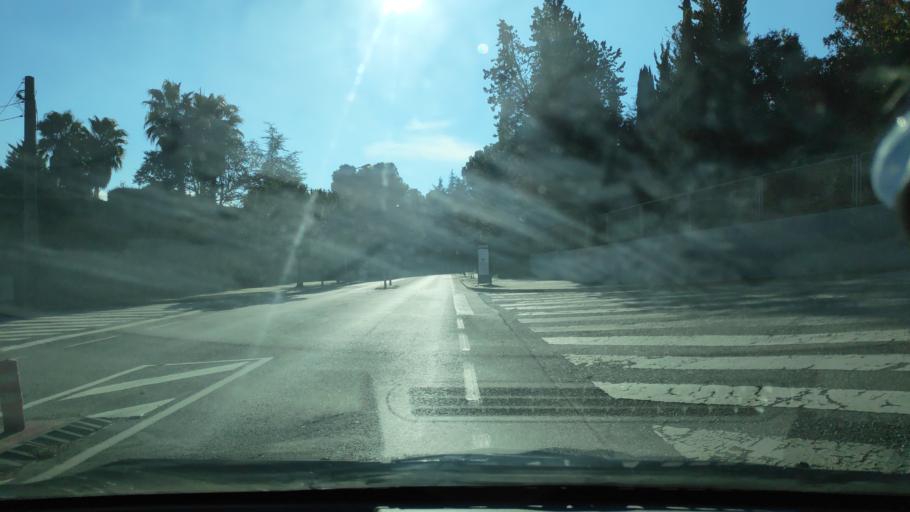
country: ES
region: Catalonia
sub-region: Provincia de Barcelona
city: Sant Quirze del Valles
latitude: 41.5074
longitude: 2.0900
